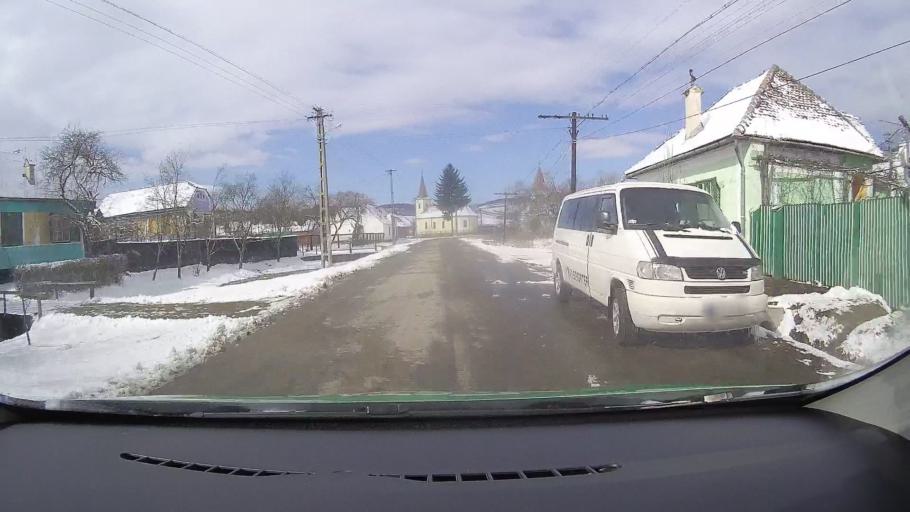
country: RO
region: Sibiu
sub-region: Comuna Altina
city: Altina
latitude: 45.9829
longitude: 24.4564
